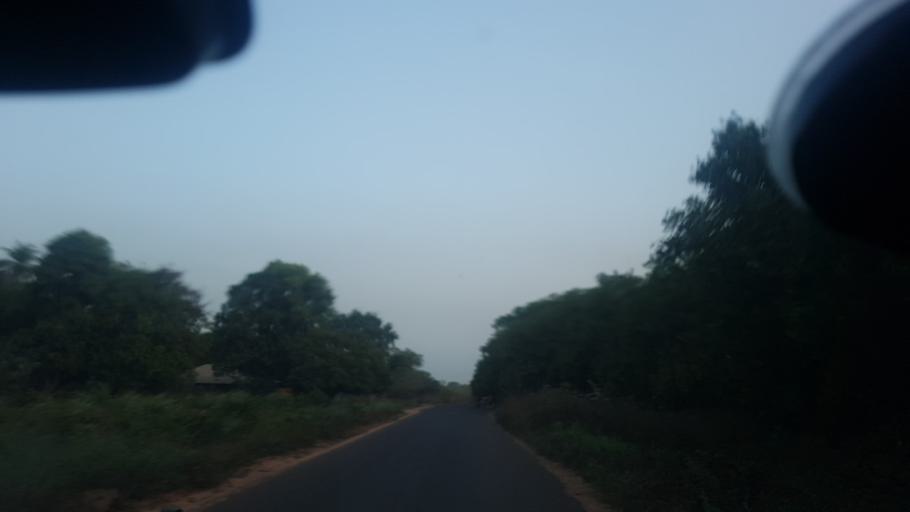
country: GW
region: Oio
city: Bissora
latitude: 12.3534
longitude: -15.7660
